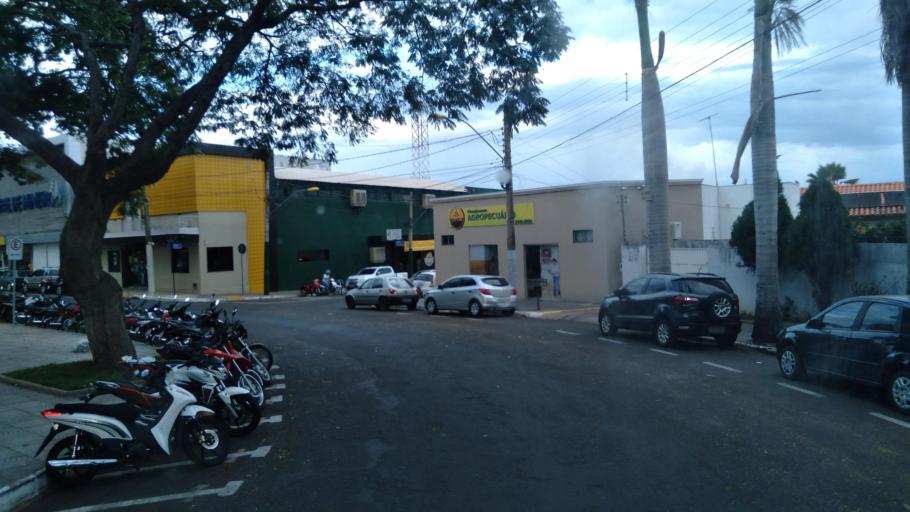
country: BR
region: Goias
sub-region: Mineiros
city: Mineiros
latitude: -17.5691
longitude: -52.5562
